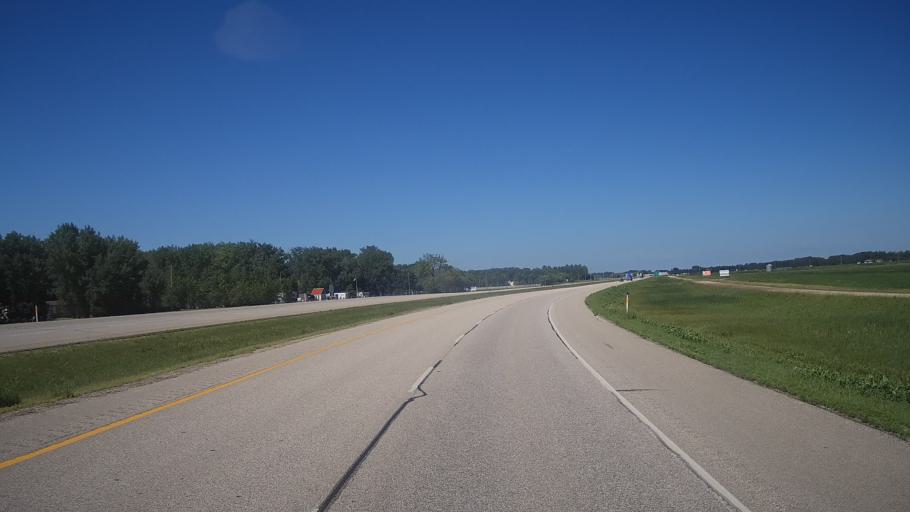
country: CA
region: Manitoba
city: Portage la Prairie
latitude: 49.9609
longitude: -98.2425
